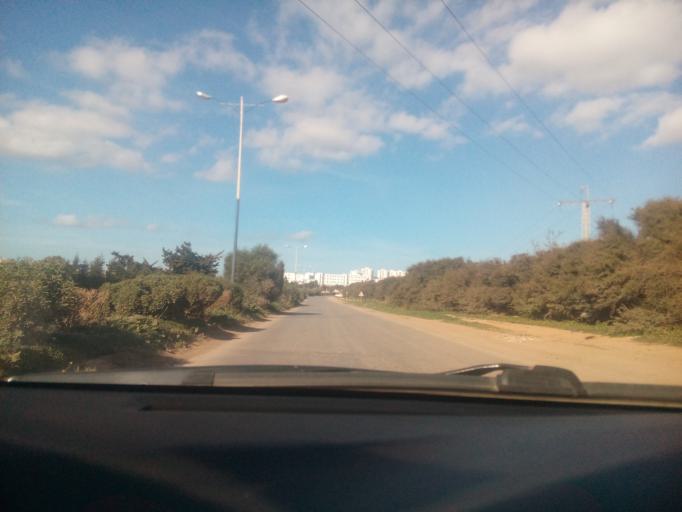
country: DZ
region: Oran
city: Bir el Djir
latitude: 35.6868
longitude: -0.5739
